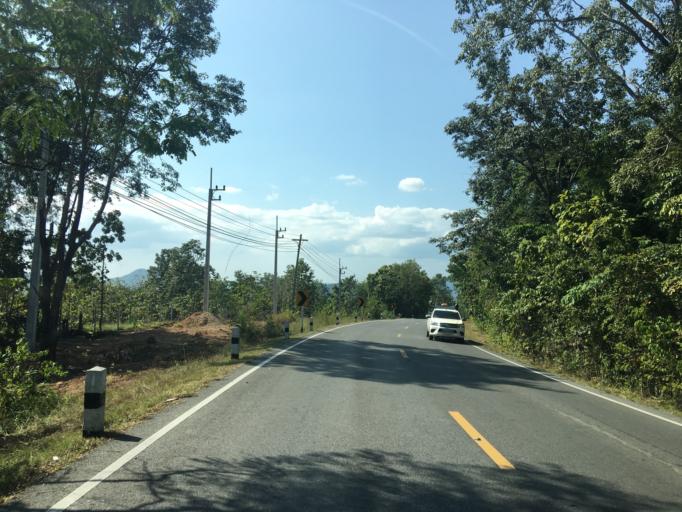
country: TH
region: Phayao
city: Chiang Muan
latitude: 18.8598
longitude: 100.3158
